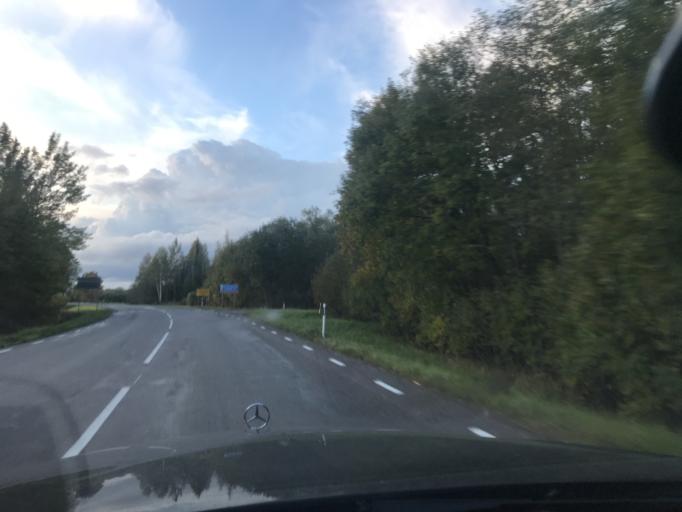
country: EE
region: Vorumaa
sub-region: Antsla vald
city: Vana-Antsla
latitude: 57.9088
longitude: 26.4191
